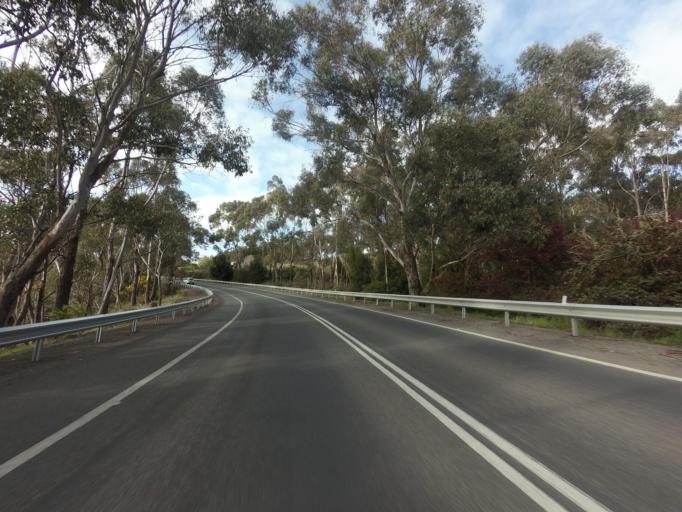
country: AU
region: Tasmania
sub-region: Huon Valley
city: Geeveston
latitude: -43.1480
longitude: 146.9779
